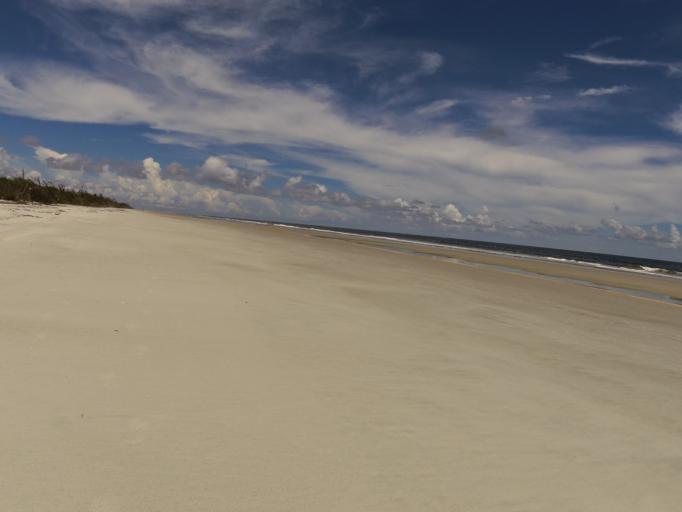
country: US
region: Florida
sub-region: Duval County
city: Atlantic Beach
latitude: 30.4704
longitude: -81.4125
